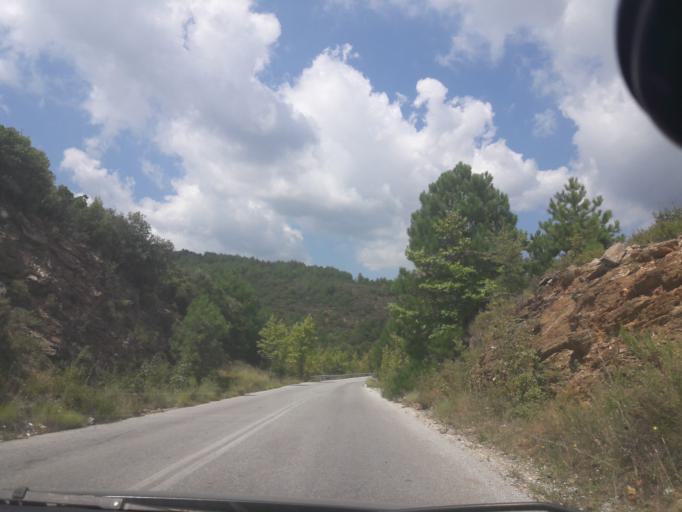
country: GR
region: Central Macedonia
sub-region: Nomos Chalkidikis
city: Polygyros
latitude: 40.3597
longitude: 23.4948
